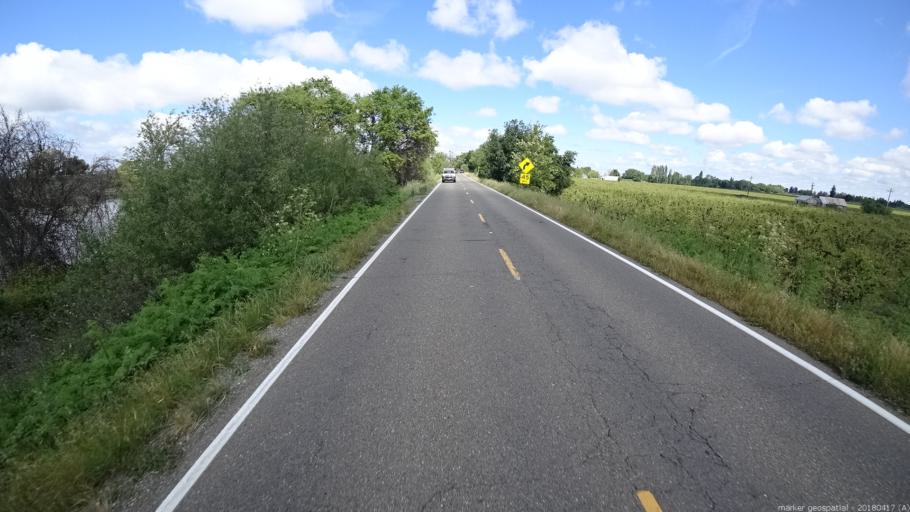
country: US
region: California
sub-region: Sacramento County
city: Walnut Grove
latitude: 38.2322
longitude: -121.5569
